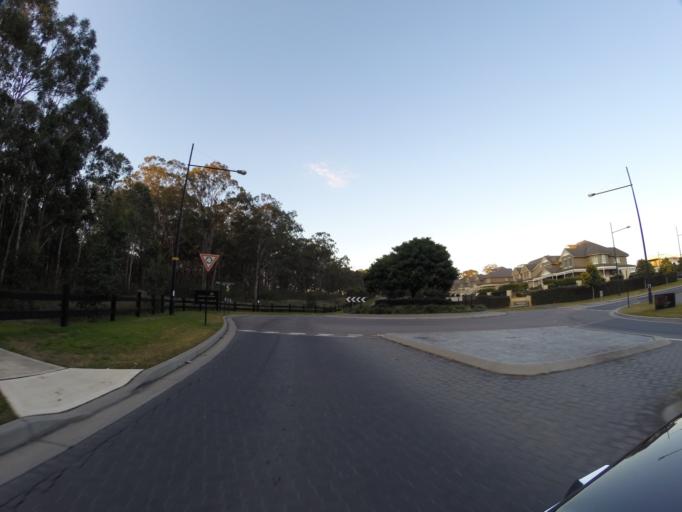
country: AU
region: New South Wales
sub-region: Camden
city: Narellan
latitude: -34.0186
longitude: 150.7421
